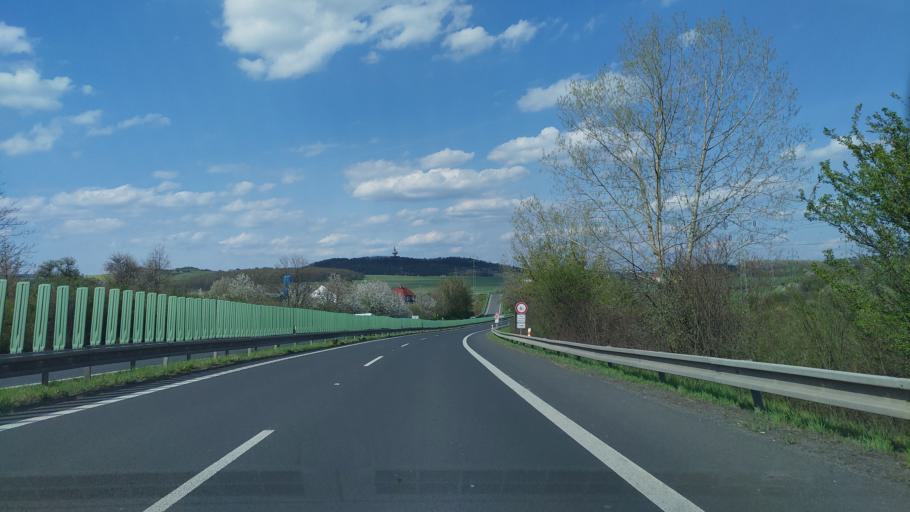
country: CZ
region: Ustecky
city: Hostomice
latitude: 50.5979
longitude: 13.8039
